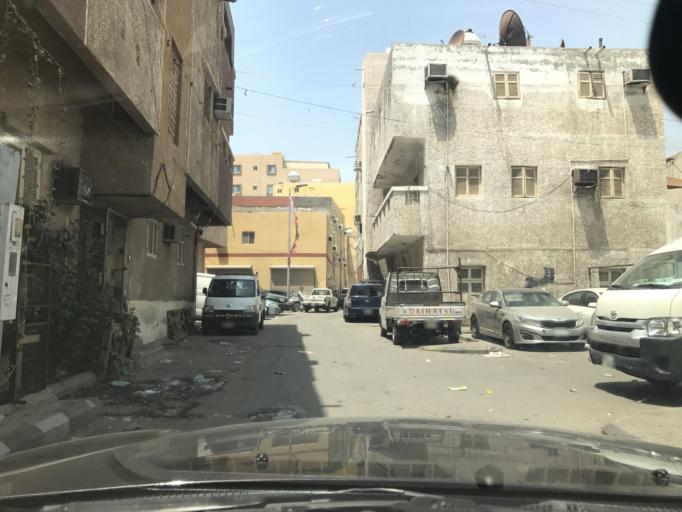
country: SA
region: Makkah
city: Jeddah
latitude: 21.4732
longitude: 39.1862
